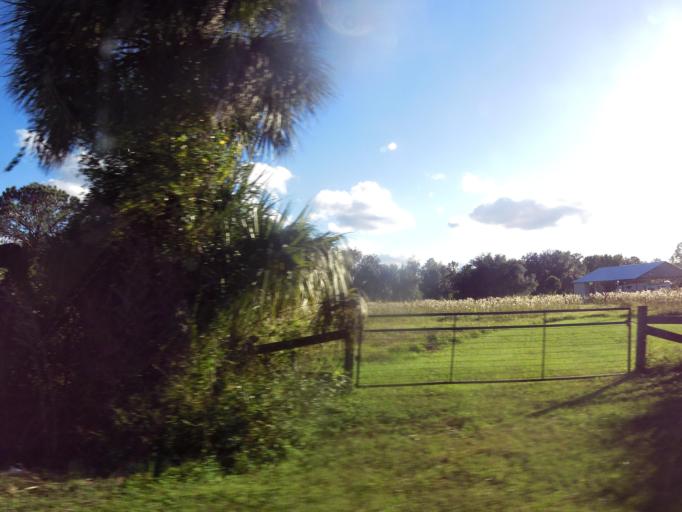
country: US
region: Florida
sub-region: Marion County
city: Citra
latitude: 29.4547
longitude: -82.1146
